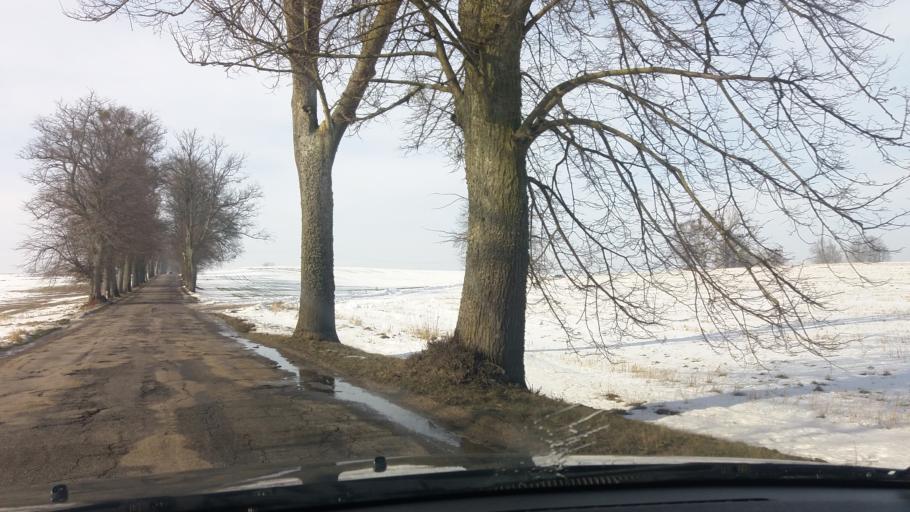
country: PL
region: Warmian-Masurian Voivodeship
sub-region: Powiat olsztynski
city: Jeziorany
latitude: 54.1011
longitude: 20.7437
